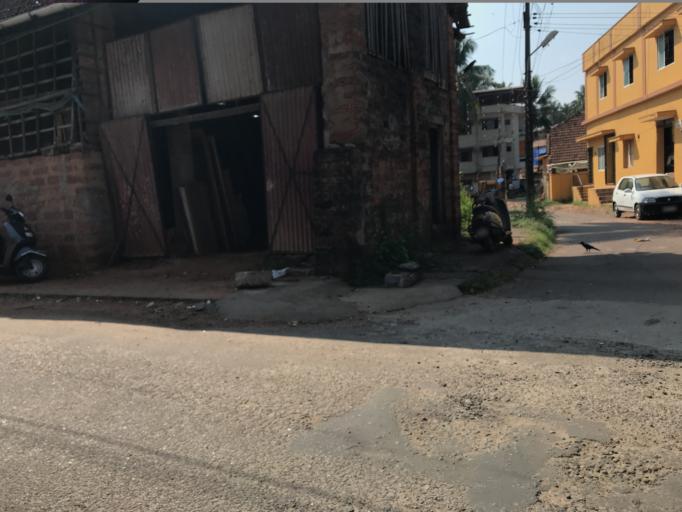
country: IN
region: Karnataka
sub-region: Dakshina Kannada
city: Mangalore
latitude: 12.8709
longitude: 74.8331
